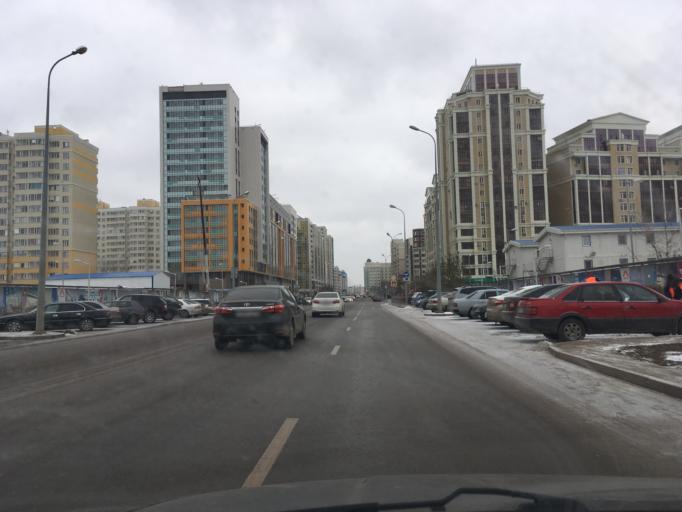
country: KZ
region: Astana Qalasy
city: Astana
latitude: 51.1163
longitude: 71.4259
